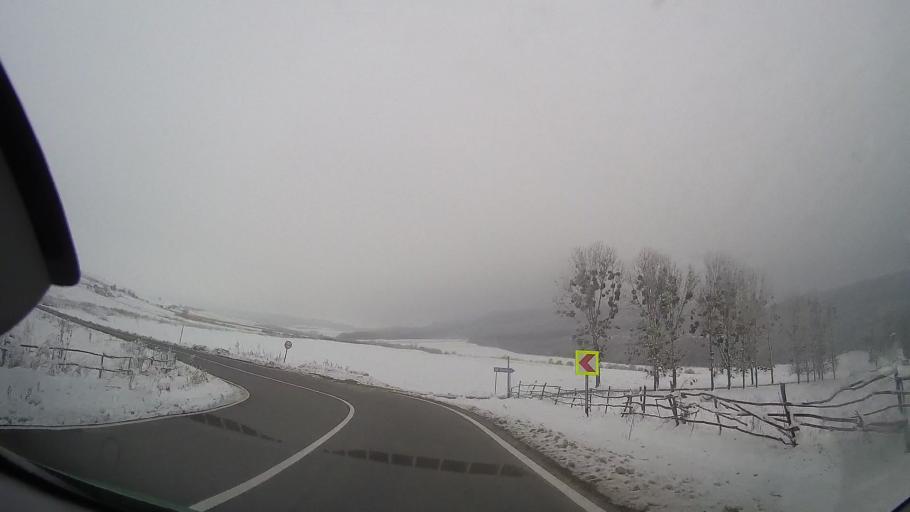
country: RO
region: Neamt
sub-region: Comuna Poenari
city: Poienari
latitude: 46.8733
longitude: 27.1368
